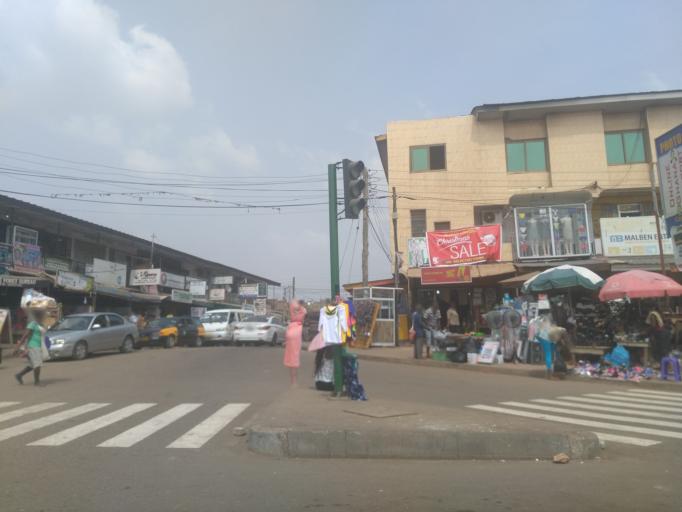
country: GH
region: Greater Accra
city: Dome
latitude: 5.6070
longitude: -0.2489
